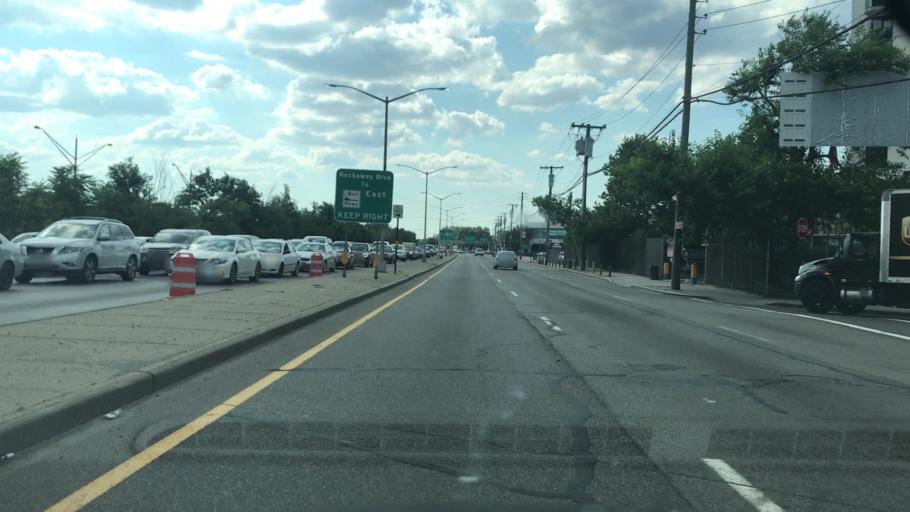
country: US
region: New York
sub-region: Nassau County
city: Inwood
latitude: 40.6573
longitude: -73.7694
